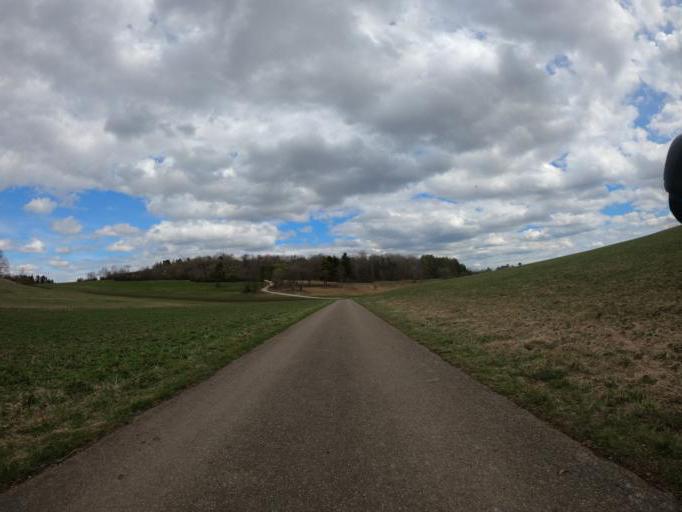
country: DE
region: Baden-Wuerttemberg
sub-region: Tuebingen Region
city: Trochtelfingen
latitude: 48.3793
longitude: 9.1743
